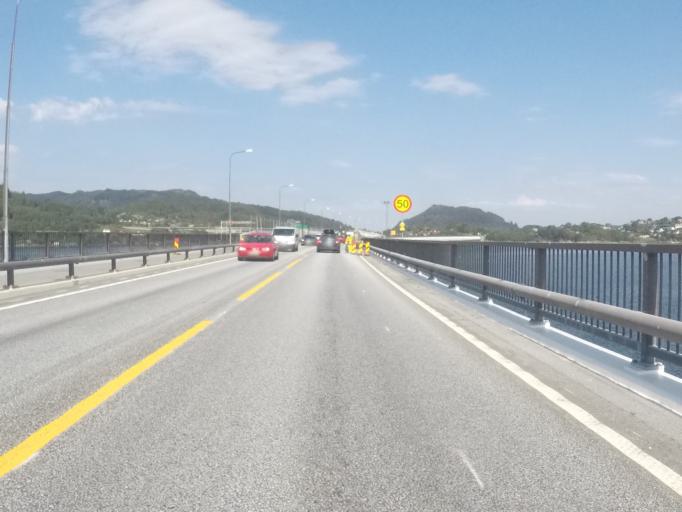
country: NO
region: Hordaland
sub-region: Meland
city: Frekhaug
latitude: 60.5235
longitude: 5.2652
